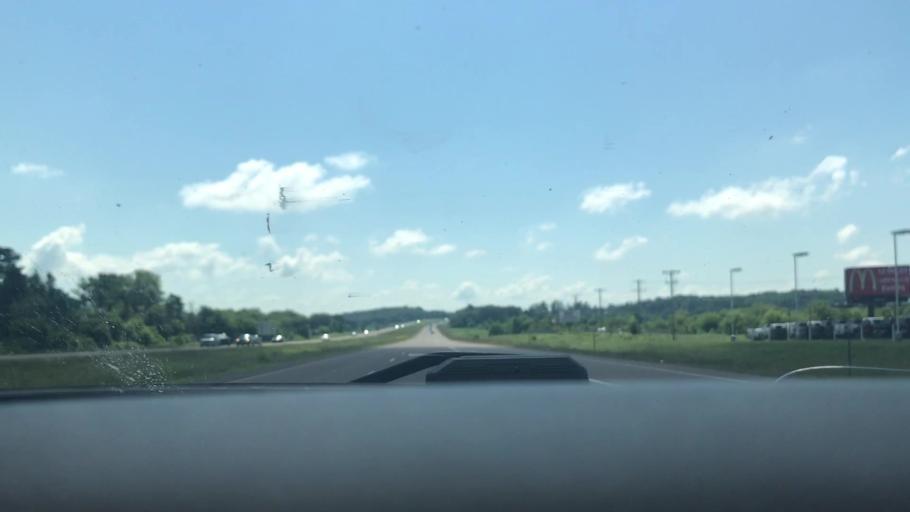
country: US
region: Wisconsin
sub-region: Chippewa County
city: Bloomer
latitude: 45.0973
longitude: -91.5010
